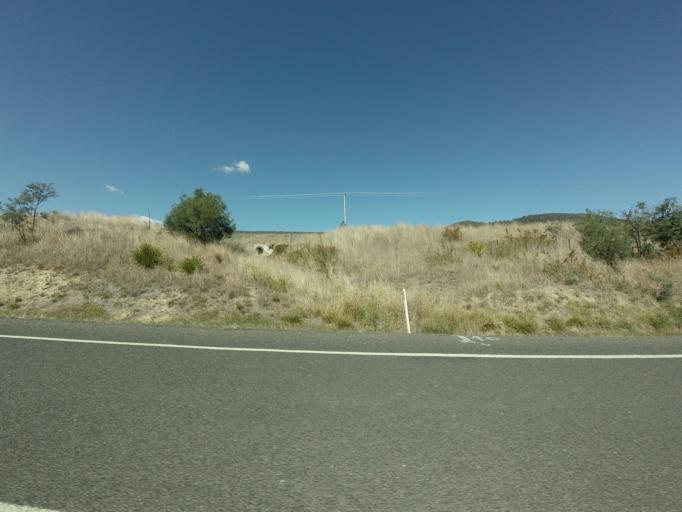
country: AU
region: Tasmania
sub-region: Break O'Day
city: St Helens
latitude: -41.7316
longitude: 147.8202
